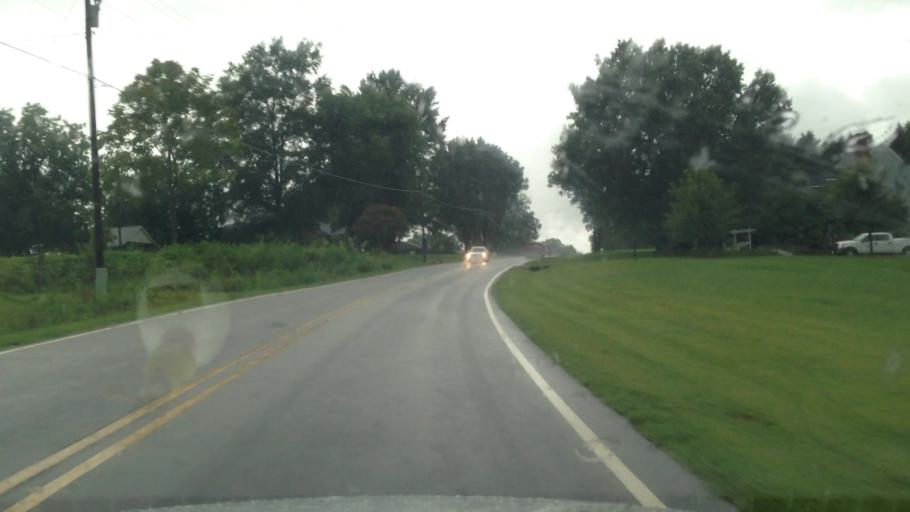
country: US
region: North Carolina
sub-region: Rockingham County
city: Reidsville
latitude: 36.2826
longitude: -79.7373
